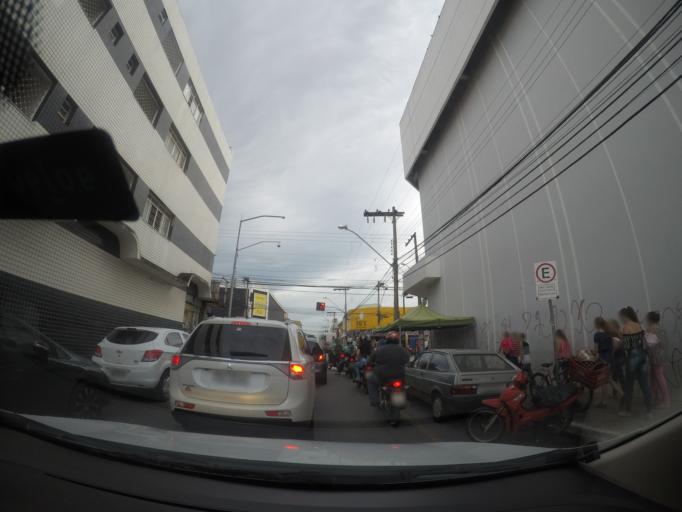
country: BR
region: Goias
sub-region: Goiania
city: Goiania
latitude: -16.6685
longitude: -49.2919
